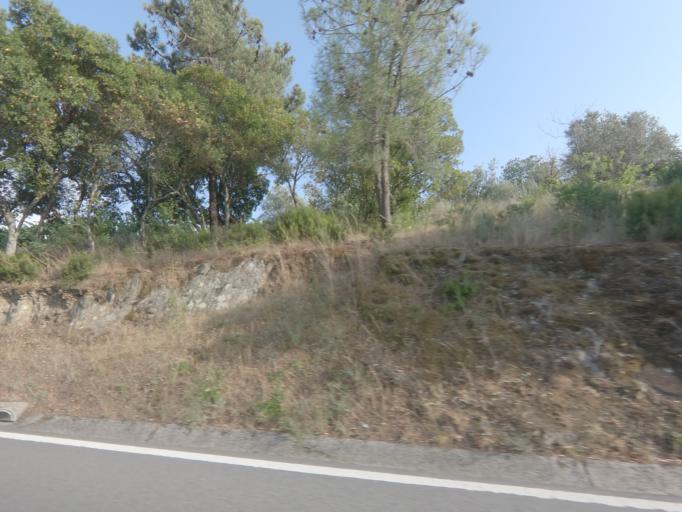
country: PT
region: Viseu
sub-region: Tabuaco
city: Tabuaco
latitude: 41.1403
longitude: -7.6036
